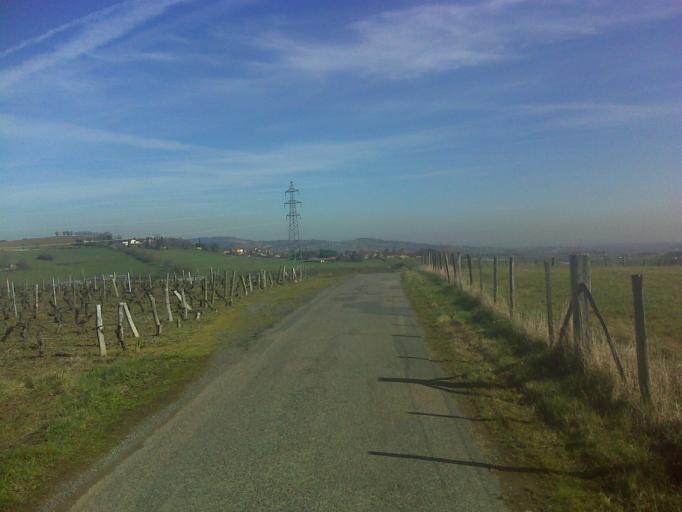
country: FR
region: Rhone-Alpes
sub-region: Departement du Rhone
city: Lentilly
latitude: 45.8207
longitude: 4.6458
